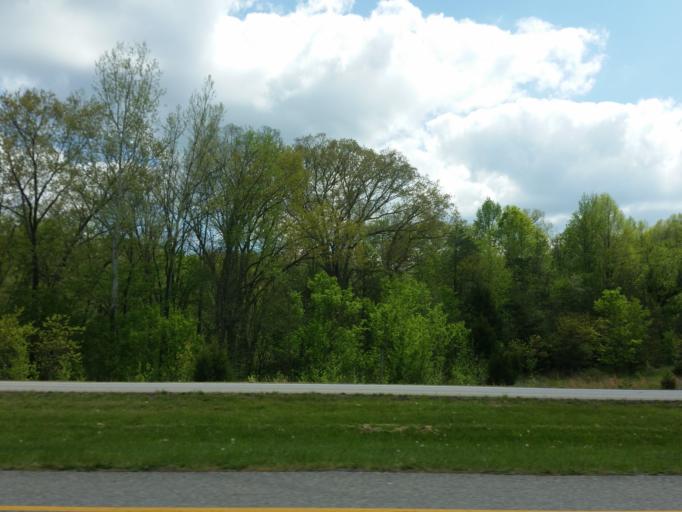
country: US
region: Kentucky
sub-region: Bell County
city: Middlesboro
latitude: 36.6054
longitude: -83.6912
